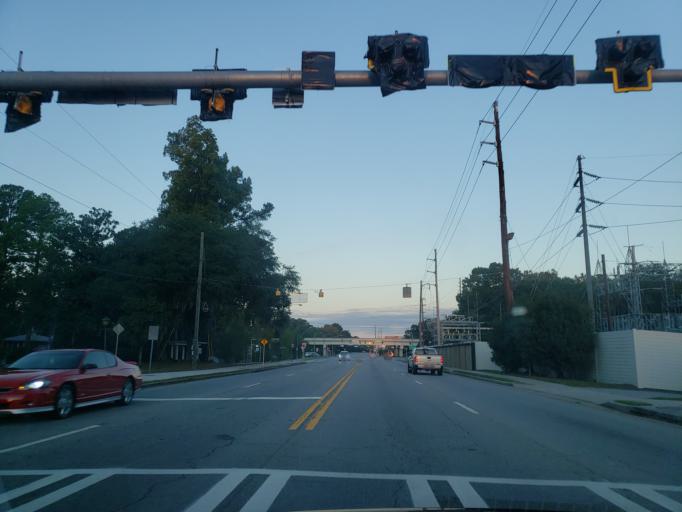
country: US
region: Georgia
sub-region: Chatham County
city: Thunderbolt
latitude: 32.0220
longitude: -81.0856
